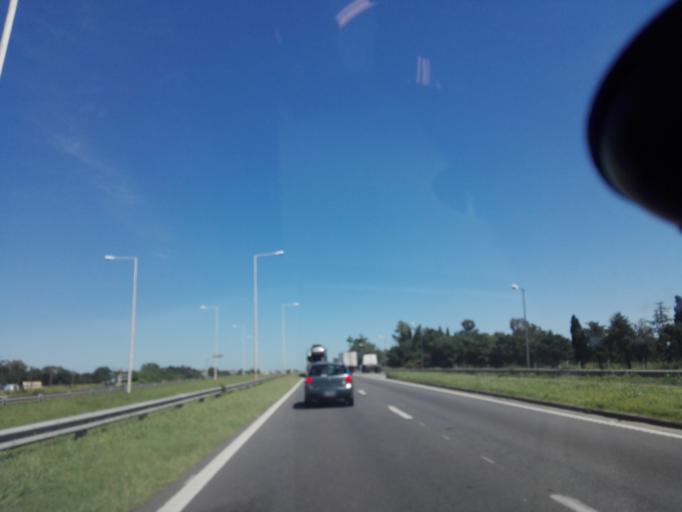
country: AR
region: Buenos Aires
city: San Nicolas de los Arroyos
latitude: -33.3860
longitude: -60.2251
